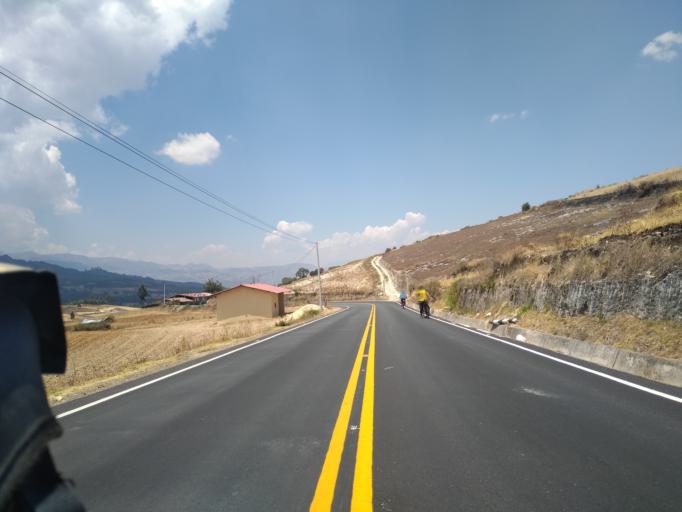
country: PE
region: Cajamarca
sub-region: San Marcos
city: San Marcos
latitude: -7.2748
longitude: -78.2471
